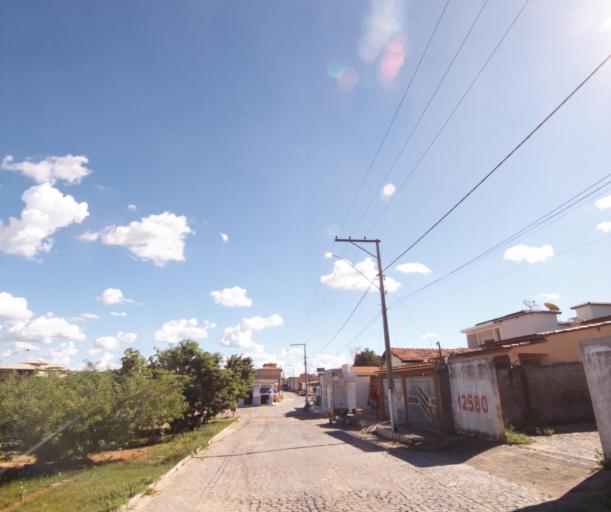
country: BR
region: Bahia
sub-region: Carinhanha
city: Carinhanha
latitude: -14.1791
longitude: -44.5315
